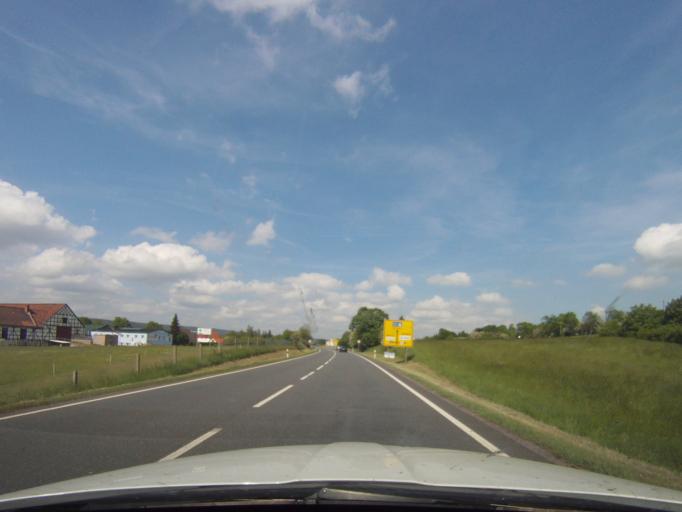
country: DE
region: Thuringia
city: Oppurg
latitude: 50.7095
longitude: 11.6565
